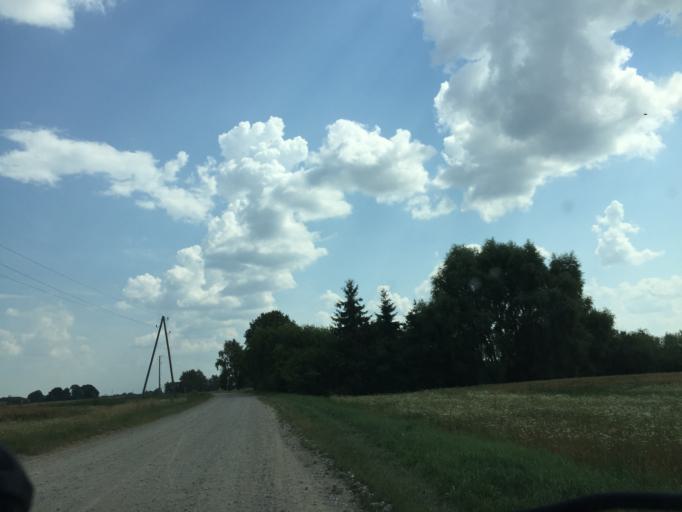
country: LT
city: Zagare
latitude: 56.3462
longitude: 23.1415
